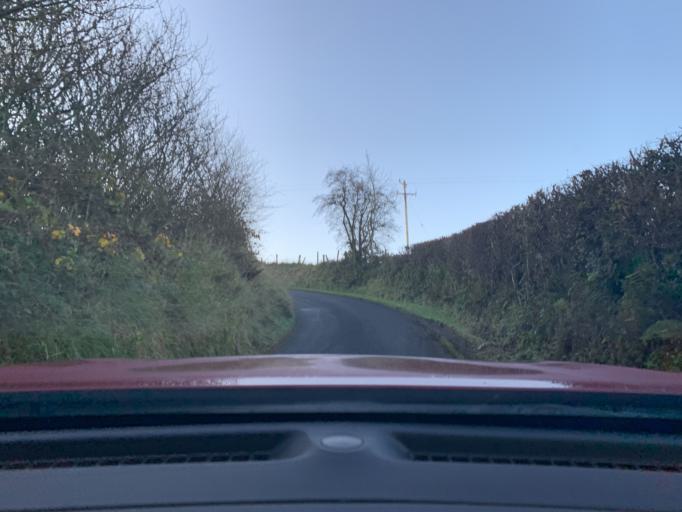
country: IE
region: Connaught
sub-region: Sligo
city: Ballymote
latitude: 54.0665
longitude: -8.5352
